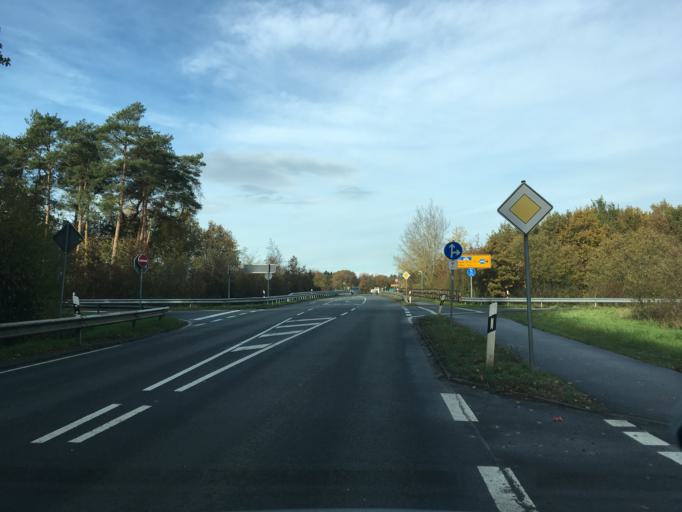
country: DE
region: North Rhine-Westphalia
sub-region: Regierungsbezirk Munster
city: Heiden
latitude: 51.8514
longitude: 6.9222
